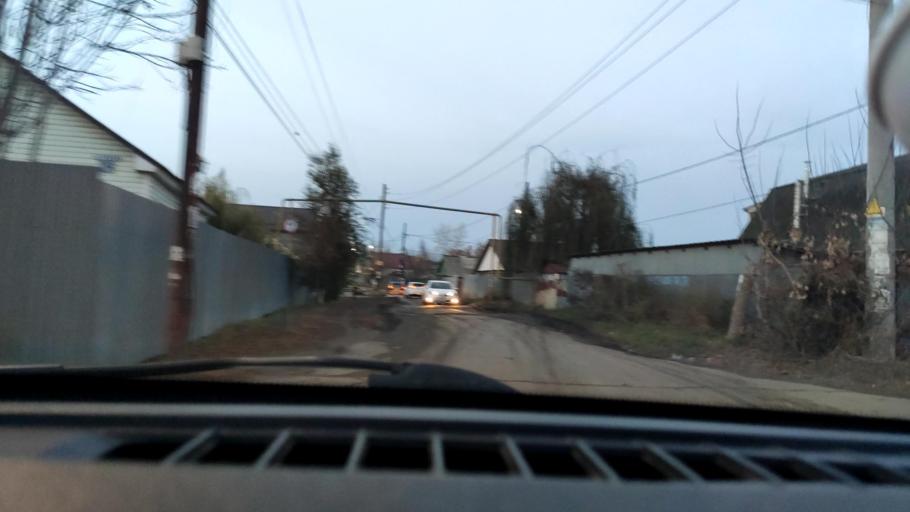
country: RU
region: Samara
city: Samara
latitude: 53.1390
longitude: 50.0961
